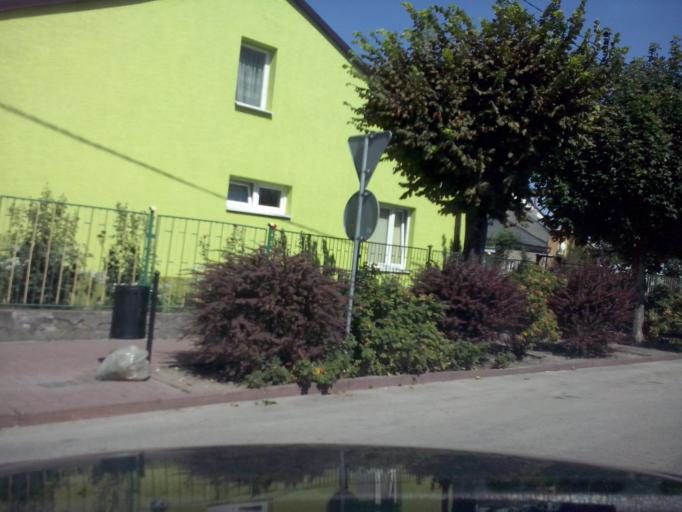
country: PL
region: Swietokrzyskie
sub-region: Powiat kielecki
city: Chmielnik
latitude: 50.6152
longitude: 20.7495
